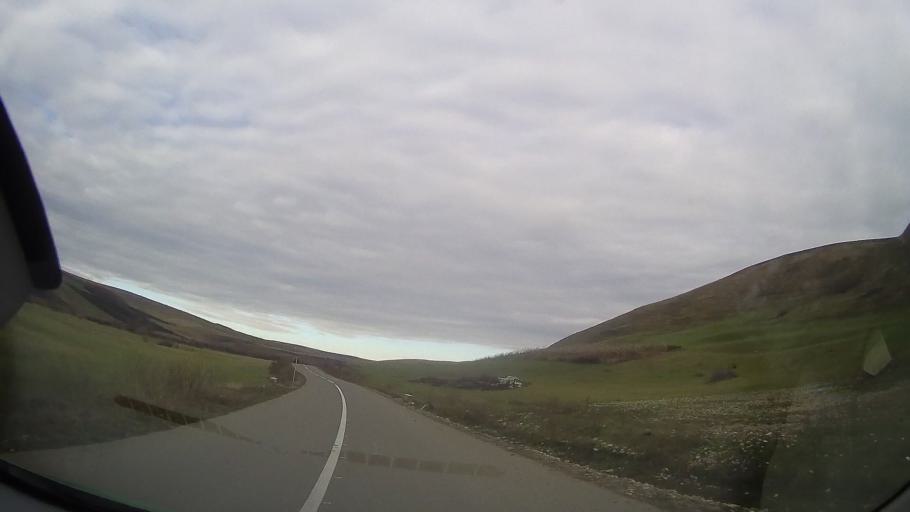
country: RO
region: Bistrita-Nasaud
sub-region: Comuna Silvasu de Campie
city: Silvasu de Campie
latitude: 46.7950
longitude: 24.2962
